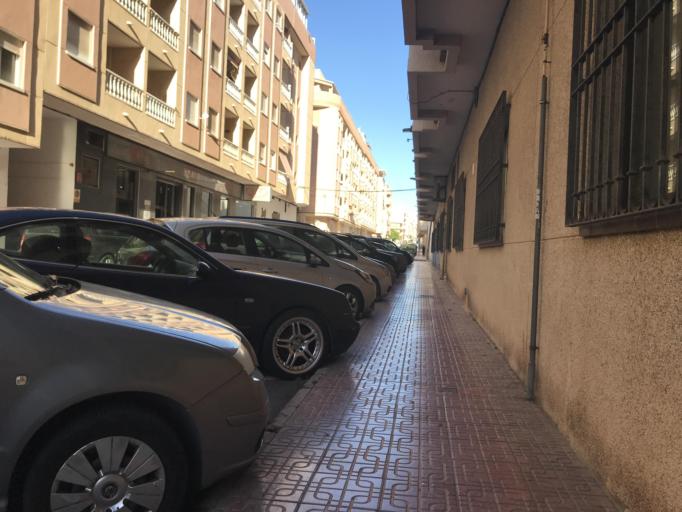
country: ES
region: Valencia
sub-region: Provincia de Alicante
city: Torrevieja
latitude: 37.9806
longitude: -0.6895
